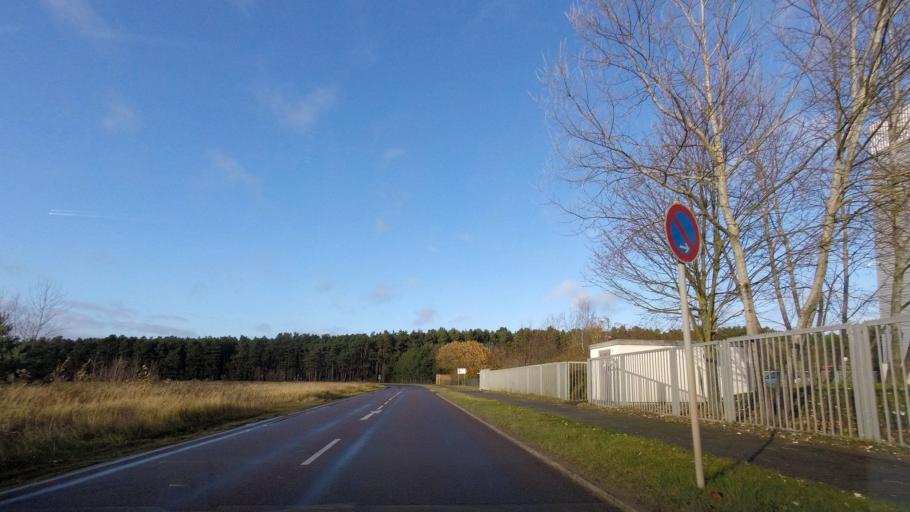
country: DE
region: Brandenburg
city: Niemegk
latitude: 52.0901
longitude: 12.7031
